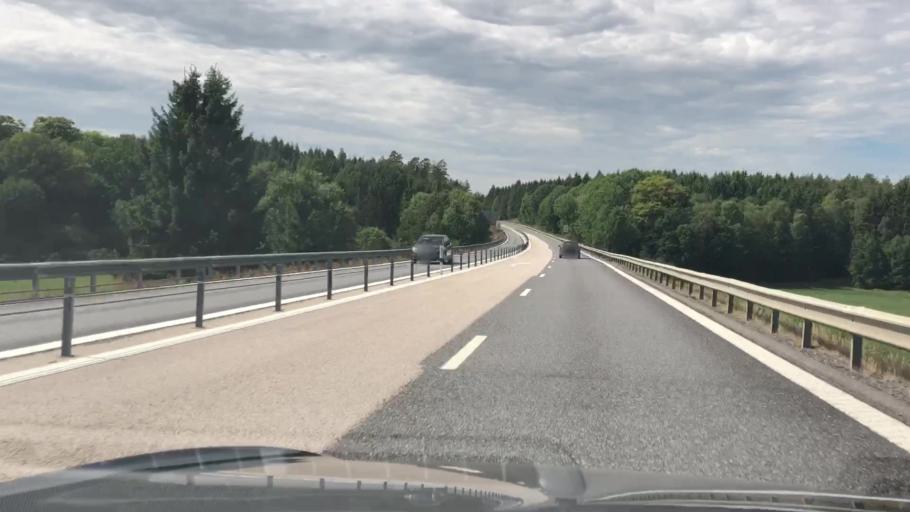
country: SE
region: Blekinge
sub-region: Ronneby Kommun
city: Ronneby
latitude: 56.2301
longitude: 15.2421
